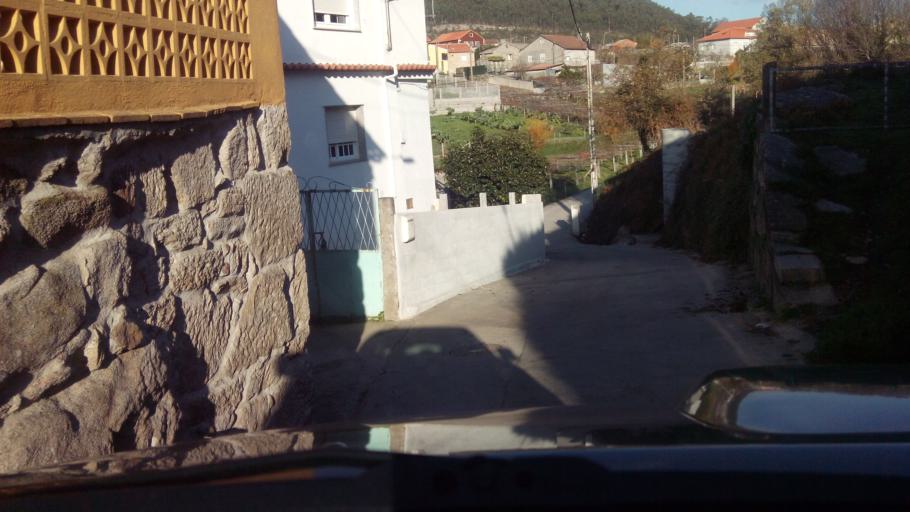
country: ES
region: Galicia
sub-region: Provincia de Pontevedra
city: Marin
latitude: 42.3613
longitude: -8.7028
